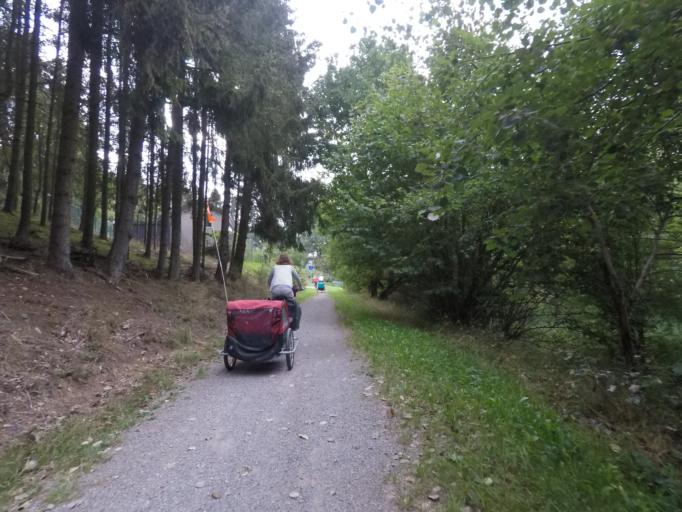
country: BE
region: Wallonia
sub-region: Province du Luxembourg
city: Martelange
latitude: 49.8452
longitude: 5.7155
